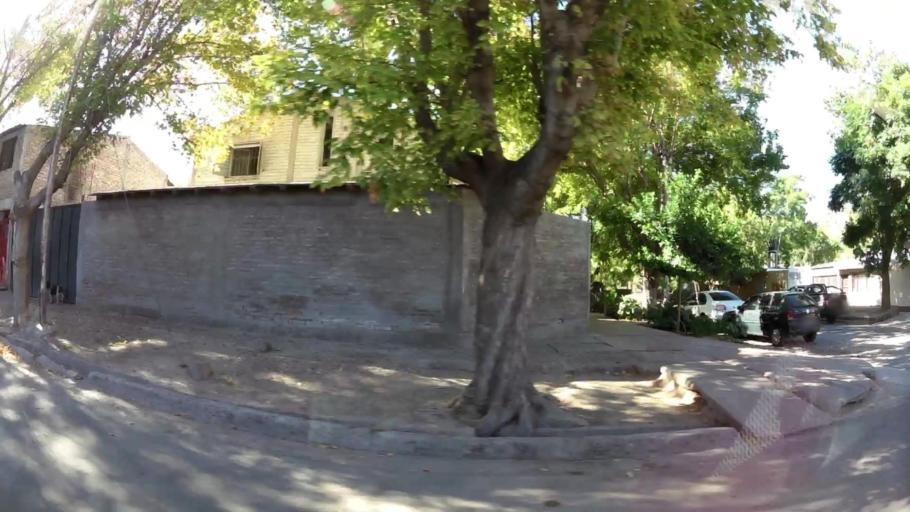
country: AR
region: Mendoza
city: Las Heras
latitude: -32.8524
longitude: -68.8280
